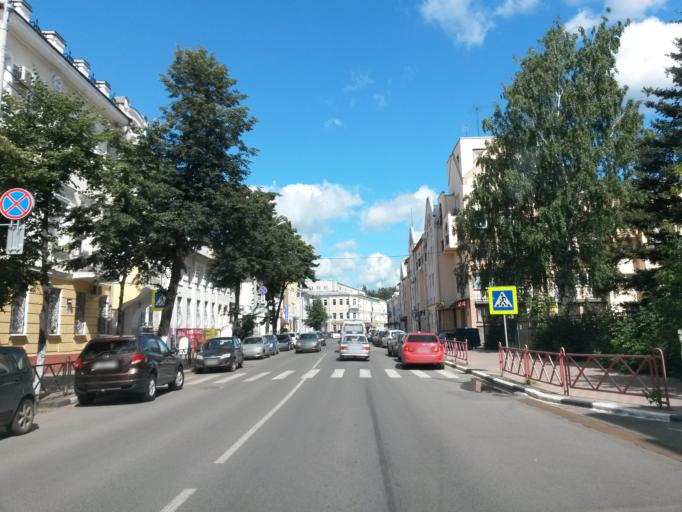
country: RU
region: Jaroslavl
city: Yaroslavl
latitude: 57.6239
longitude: 39.8816
